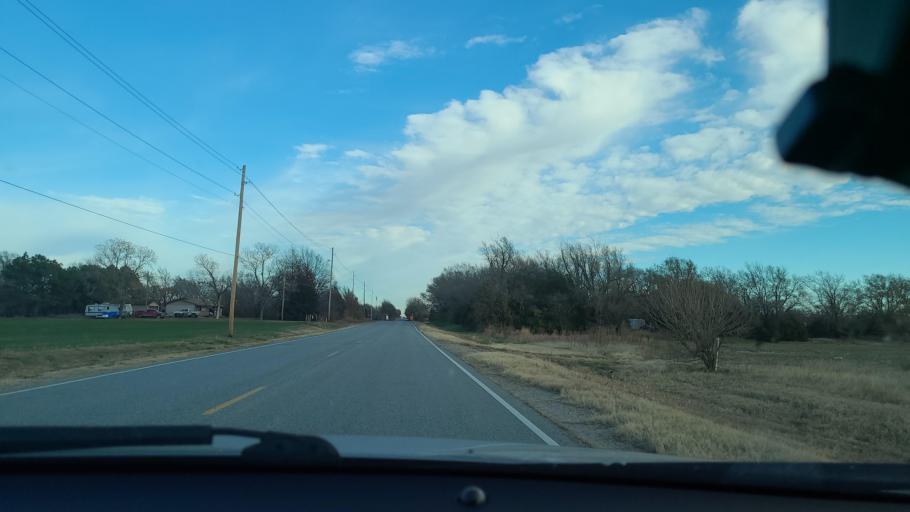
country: US
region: Kansas
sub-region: Sedgwick County
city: Goddard
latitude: 37.6496
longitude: -97.5569
